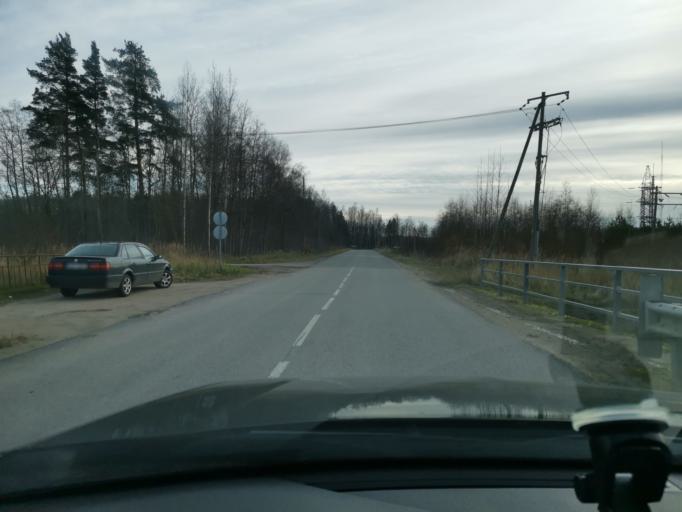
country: EE
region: Ida-Virumaa
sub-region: Sillamaee linn
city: Sillamae
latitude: 59.2726
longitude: 27.9121
